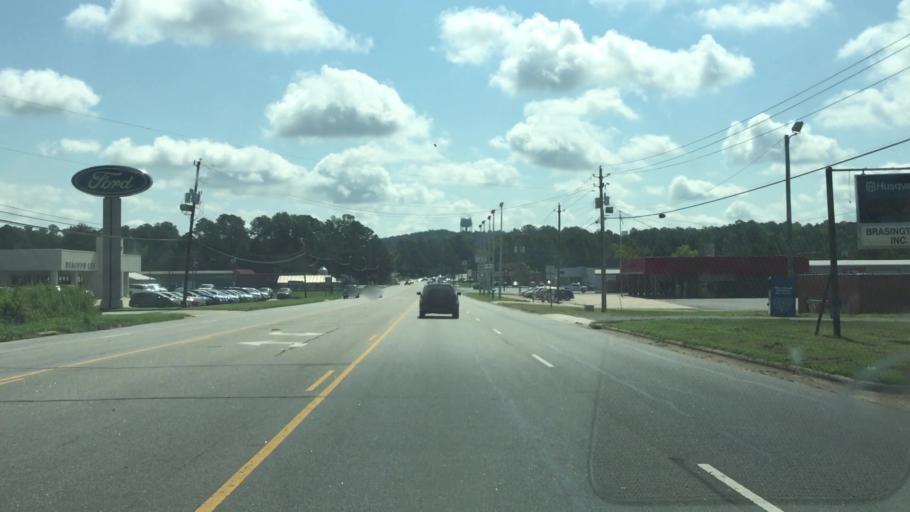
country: US
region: North Carolina
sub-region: Anson County
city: Wadesboro
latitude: 34.9787
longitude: -80.0960
